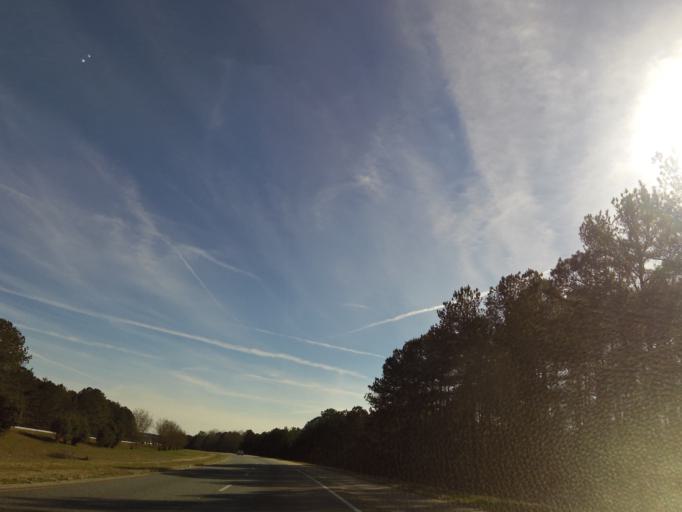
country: US
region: Georgia
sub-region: Troup County
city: La Grange
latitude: 32.9439
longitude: -84.9573
